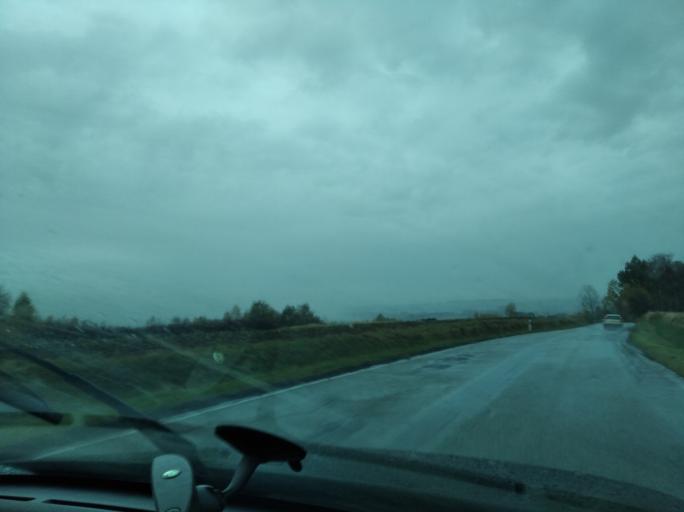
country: PL
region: Subcarpathian Voivodeship
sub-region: Powiat lancucki
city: Handzlowka
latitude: 50.0022
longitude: 22.2022
